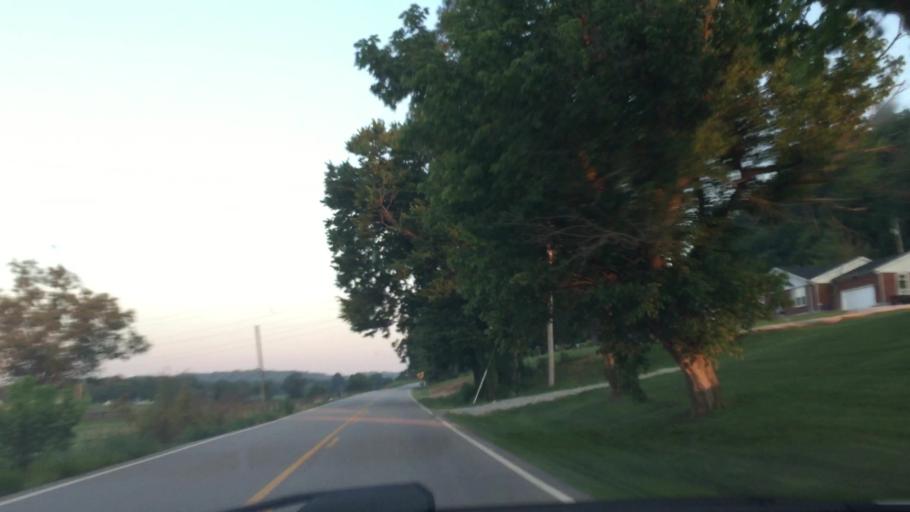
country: US
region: Kentucky
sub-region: Carroll County
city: Carrollton
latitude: 38.6413
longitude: -85.1433
